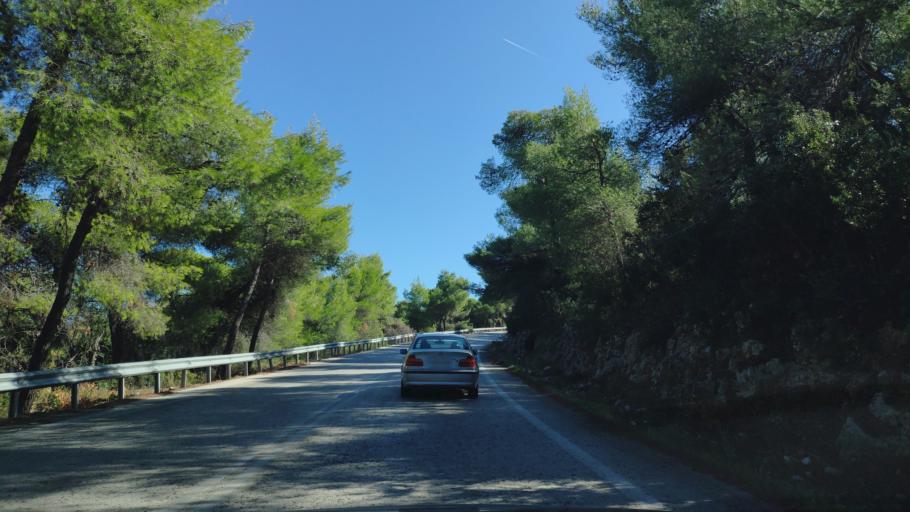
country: GR
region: Peloponnese
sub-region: Nomos Korinthias
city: Sofikon
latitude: 37.8262
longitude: 23.1004
